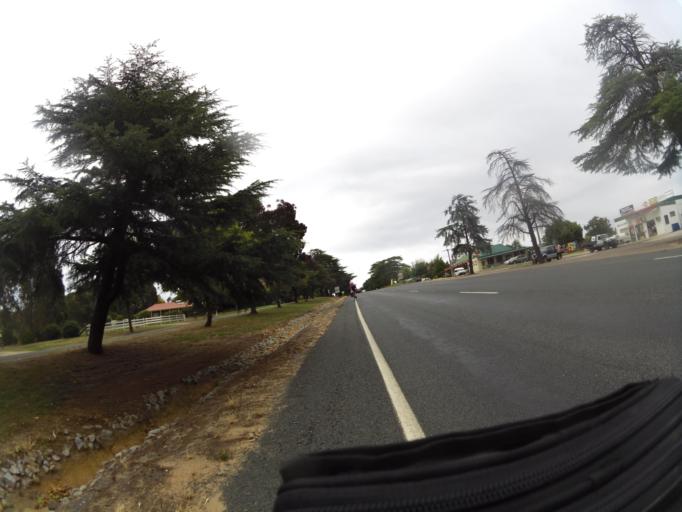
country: AU
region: New South Wales
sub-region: Snowy River
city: Jindabyne
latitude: -36.1907
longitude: 147.9125
